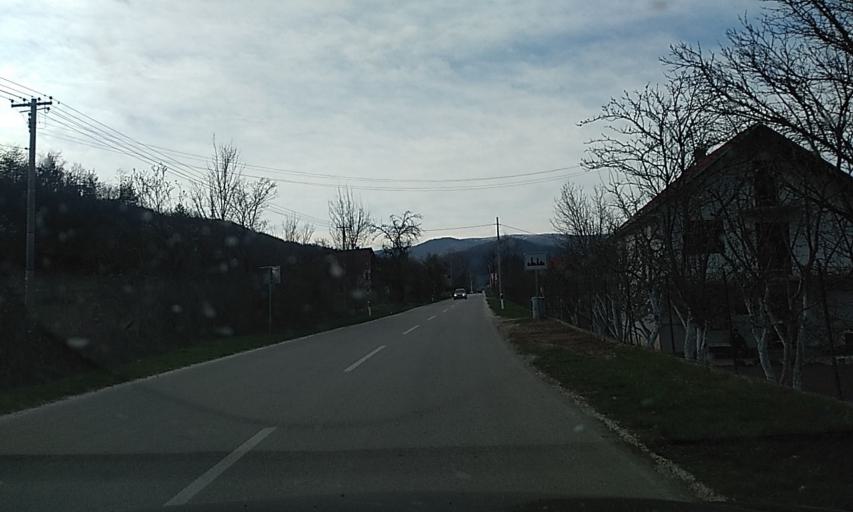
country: RS
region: Central Serbia
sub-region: Pcinjski Okrug
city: Bosilegrad
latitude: 42.4748
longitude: 22.4800
